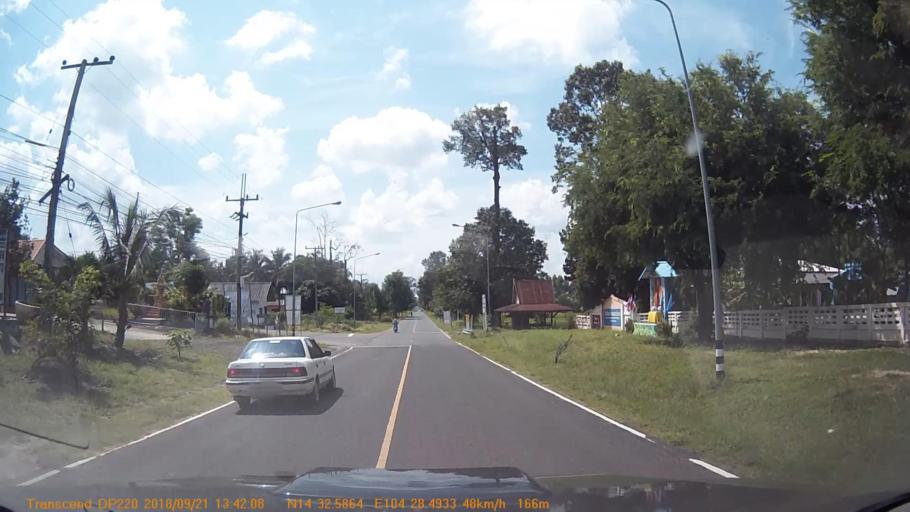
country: TH
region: Sisaket
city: Khun Han
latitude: 14.5433
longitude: 104.4745
